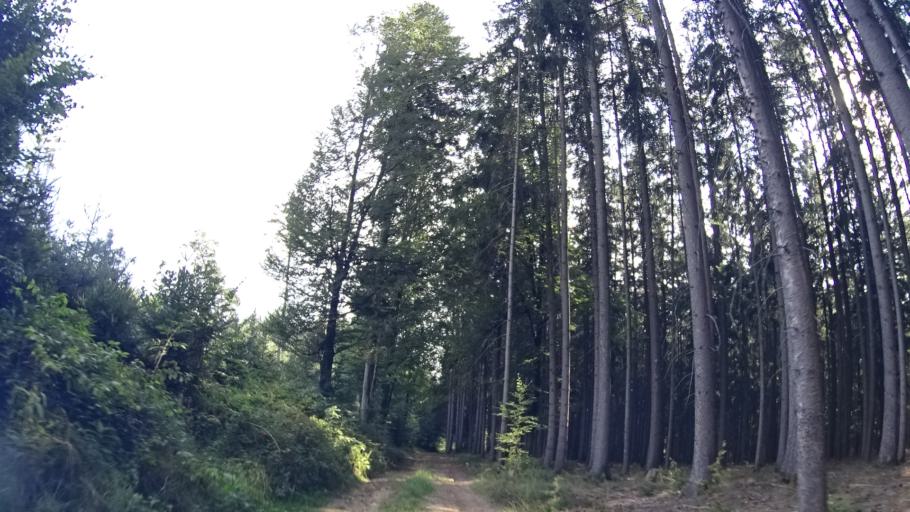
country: DE
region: Bavaria
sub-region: Upper Bavaria
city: Mindelstetten
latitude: 48.9146
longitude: 11.6396
